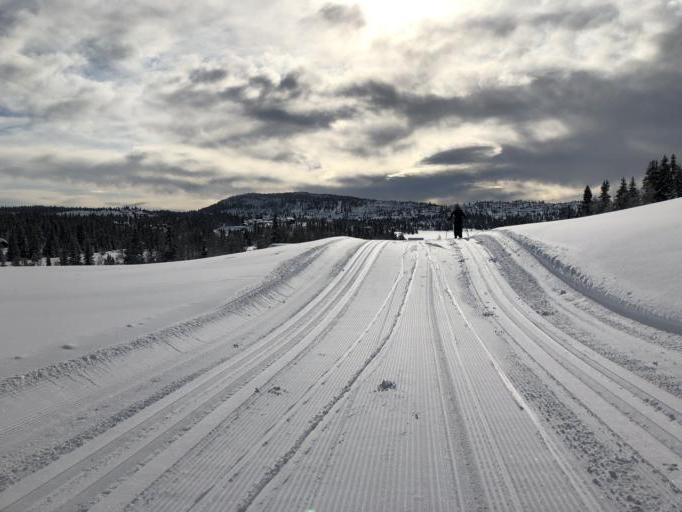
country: NO
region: Oppland
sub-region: Gausdal
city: Segalstad bru
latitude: 61.3188
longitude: 10.0582
